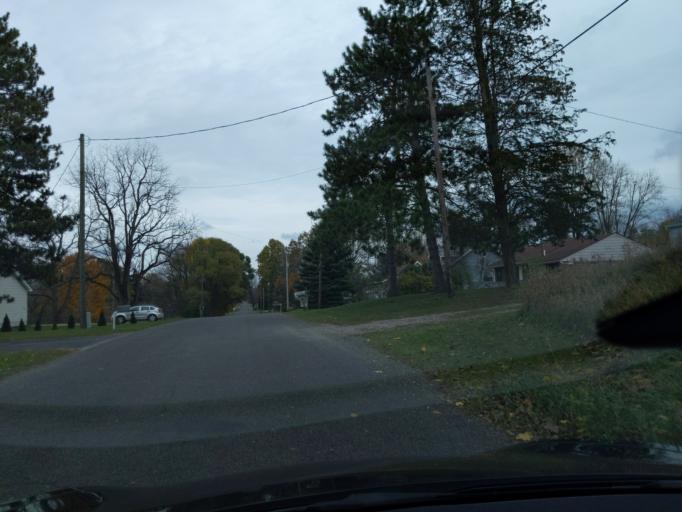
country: US
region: Michigan
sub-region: Ingham County
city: Lansing
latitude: 42.7807
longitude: -84.5539
